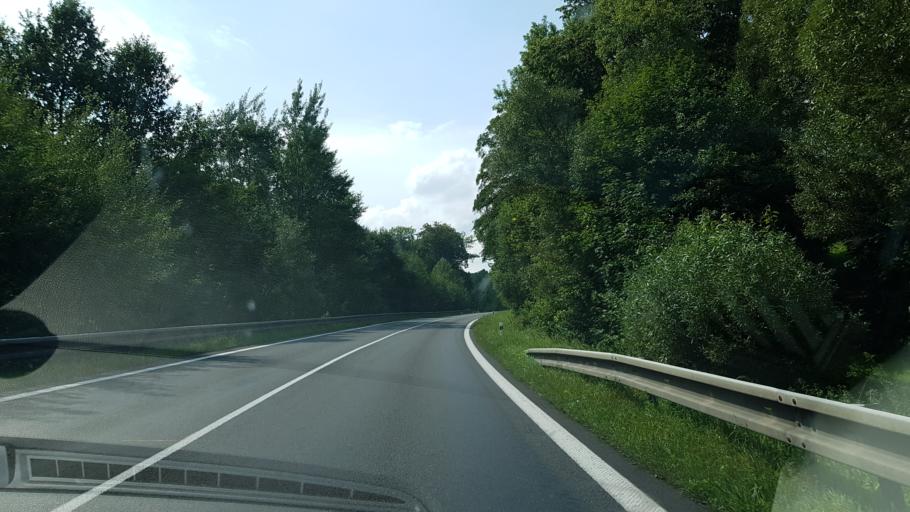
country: CZ
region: Olomoucky
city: Mikulovice
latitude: 50.2976
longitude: 17.3116
